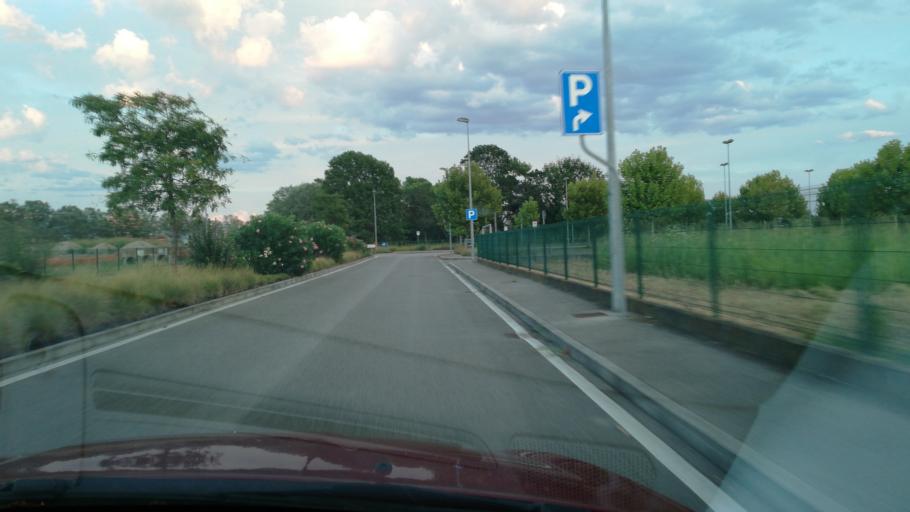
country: IT
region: Veneto
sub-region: Provincia di Venezia
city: Caorle
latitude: 45.5822
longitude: 12.8353
